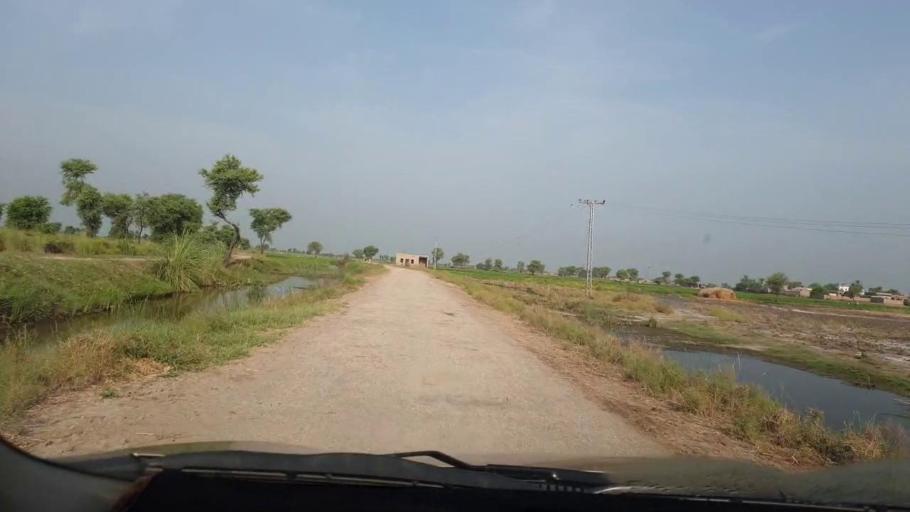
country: PK
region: Sindh
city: Goth Garelo
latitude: 27.4837
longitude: 68.0689
